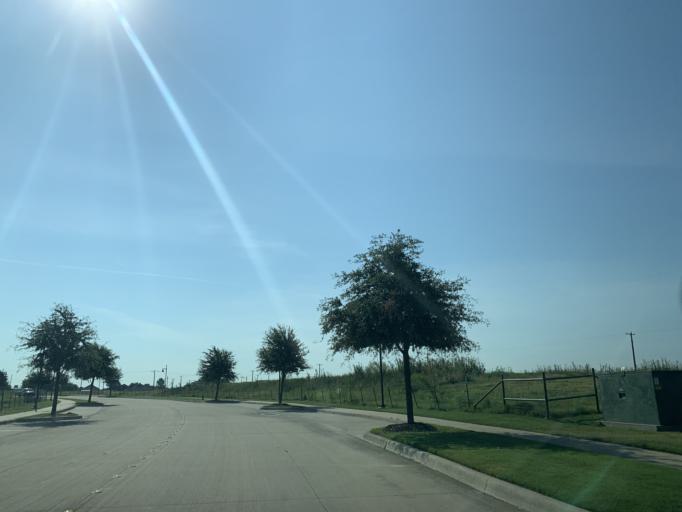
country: US
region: Texas
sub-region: Tarrant County
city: Blue Mound
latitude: 32.8924
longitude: -97.3110
